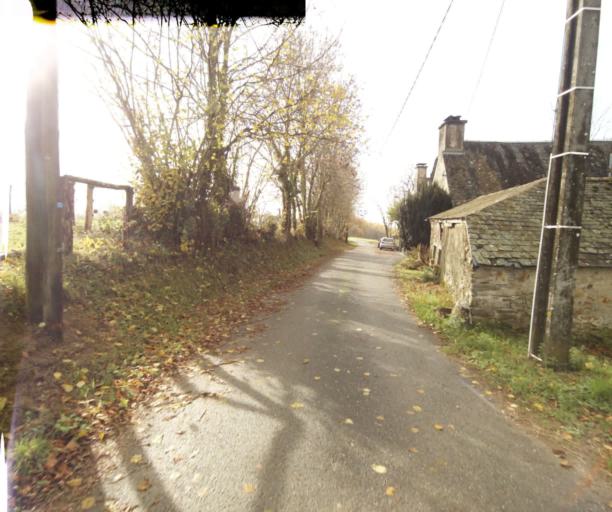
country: FR
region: Limousin
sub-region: Departement de la Correze
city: Sainte-Fereole
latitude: 45.2257
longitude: 1.6264
